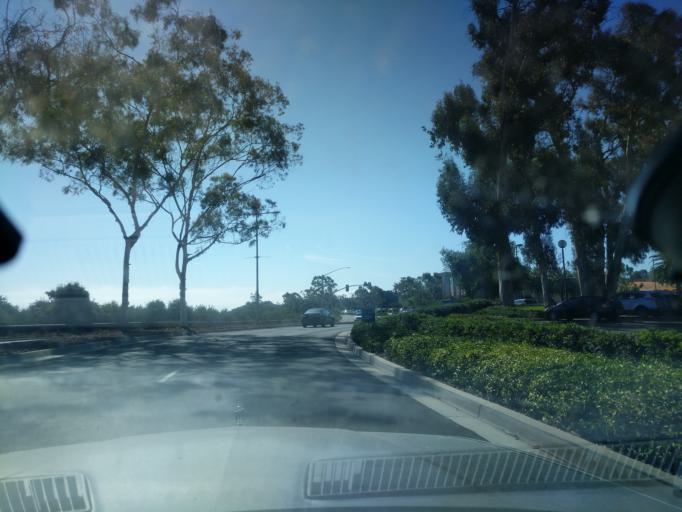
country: US
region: California
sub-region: Santa Barbara County
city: Isla Vista
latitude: 34.4186
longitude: -119.8466
